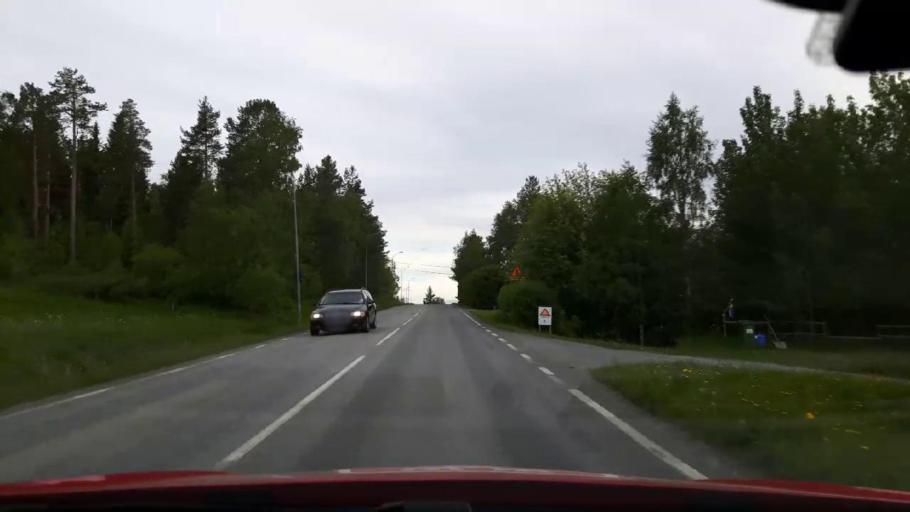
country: SE
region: Jaemtland
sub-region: OEstersunds Kommun
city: Ostersund
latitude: 63.1521
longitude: 14.4899
